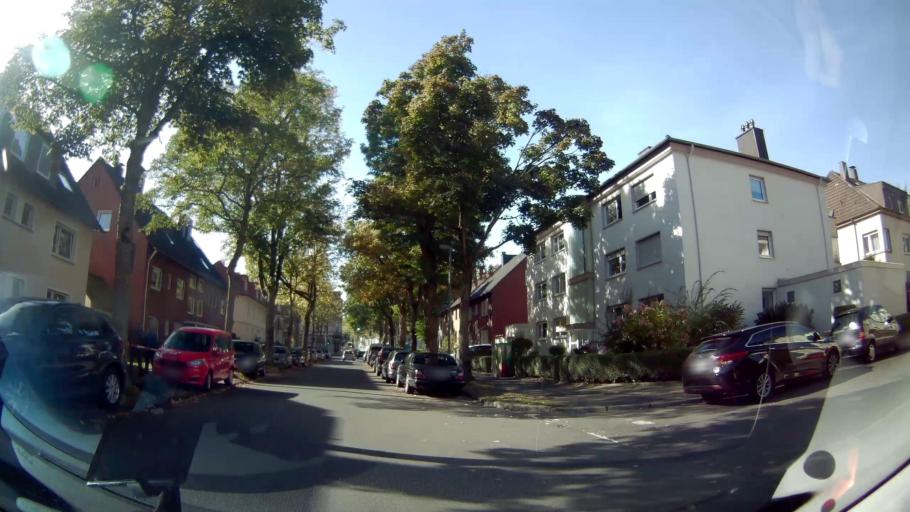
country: DE
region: North Rhine-Westphalia
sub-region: Regierungsbezirk Arnsberg
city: Bochum
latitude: 51.4663
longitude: 7.2137
